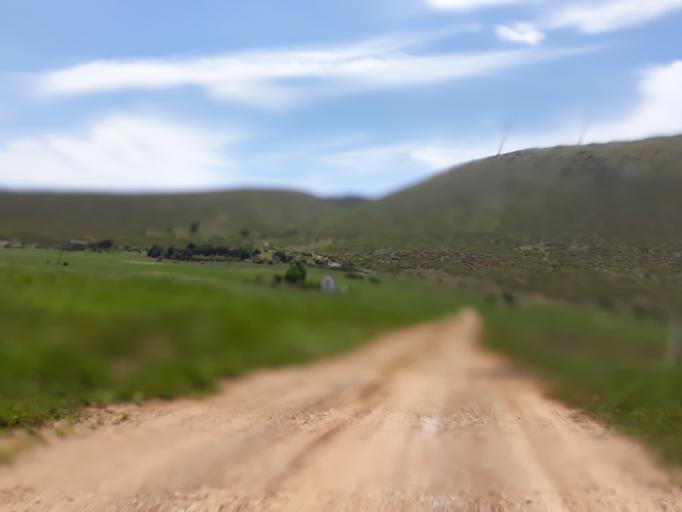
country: GR
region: Central Greece
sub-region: Nomos Voiotias
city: Ayios Thomas
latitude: 38.1845
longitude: 23.5617
